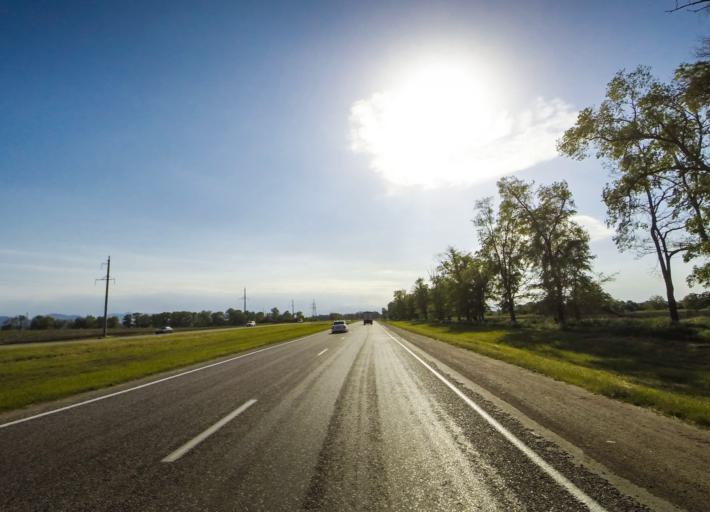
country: RU
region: Kabardino-Balkariya
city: Nartan
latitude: 43.5029
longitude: 43.7260
